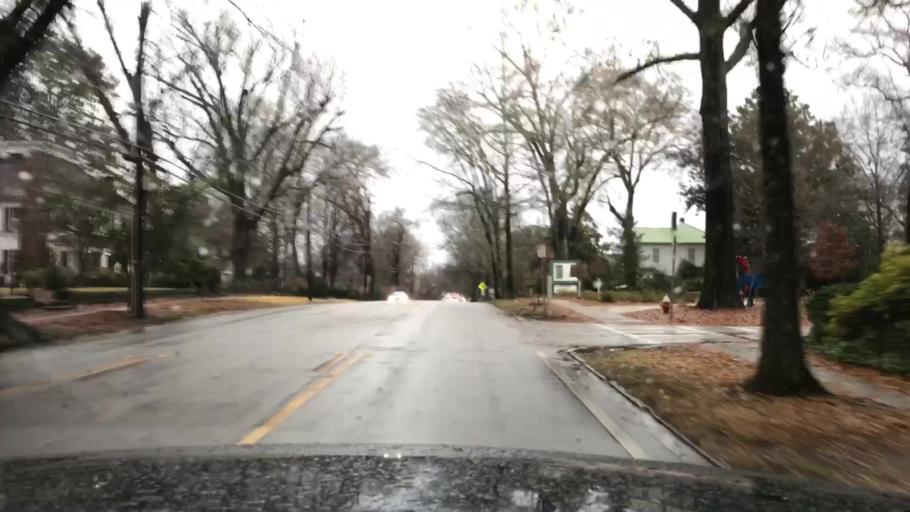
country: US
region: Georgia
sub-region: Morgan County
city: Madison
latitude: 33.5917
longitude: -83.4721
